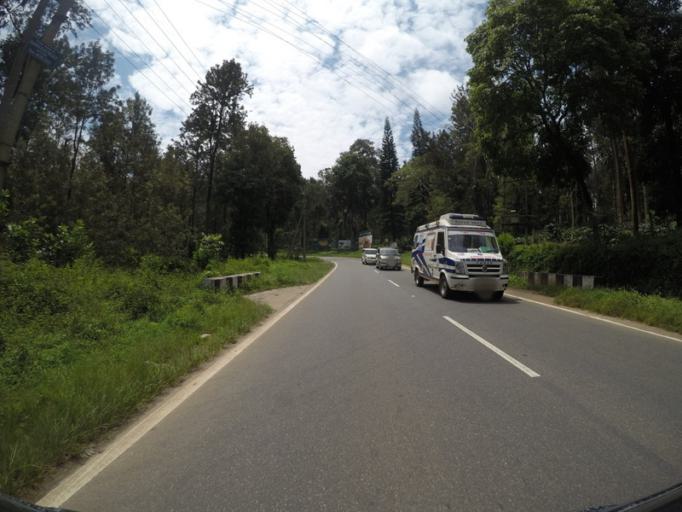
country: IN
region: Karnataka
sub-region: Kodagu
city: Suntikoppa
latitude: 12.4491
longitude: 75.8377
